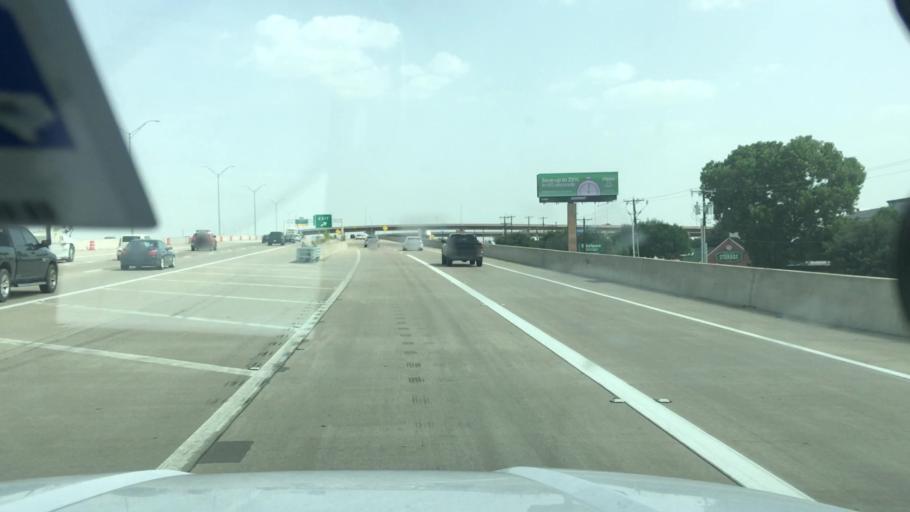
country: US
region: Texas
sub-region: Tarrant County
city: Grapevine
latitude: 32.9347
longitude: -97.0973
